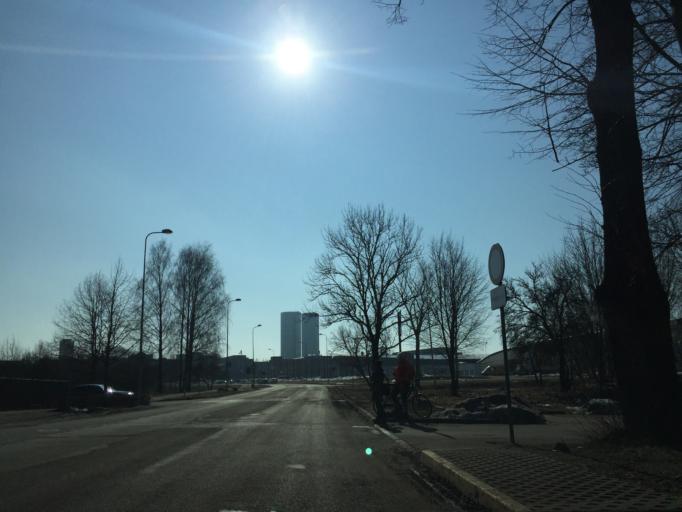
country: LV
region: Riga
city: Riga
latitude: 56.9572
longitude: 24.0809
